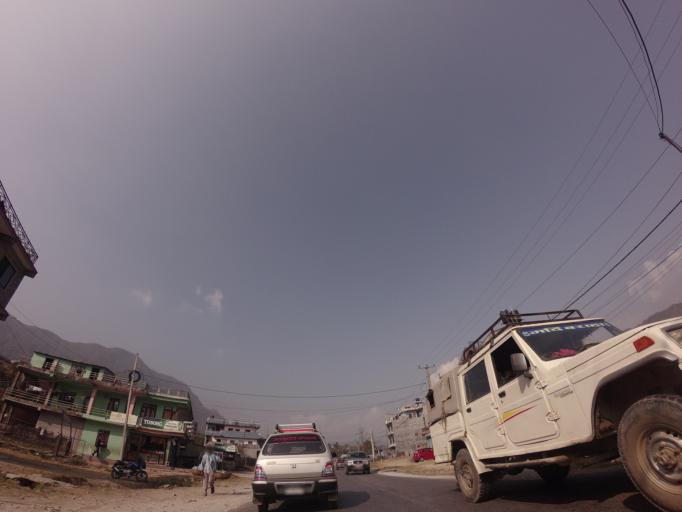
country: NP
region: Western Region
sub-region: Gandaki Zone
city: Pokhara
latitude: 28.2574
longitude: 83.9631
